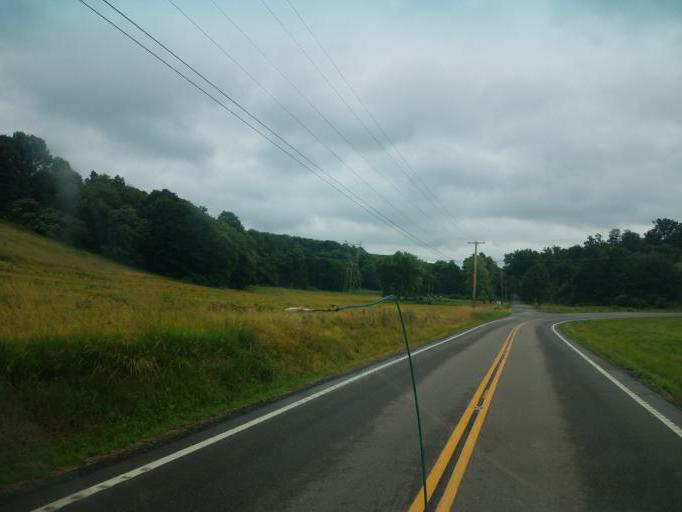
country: US
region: Ohio
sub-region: Stark County
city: Minerva
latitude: 40.7039
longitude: -81.0092
